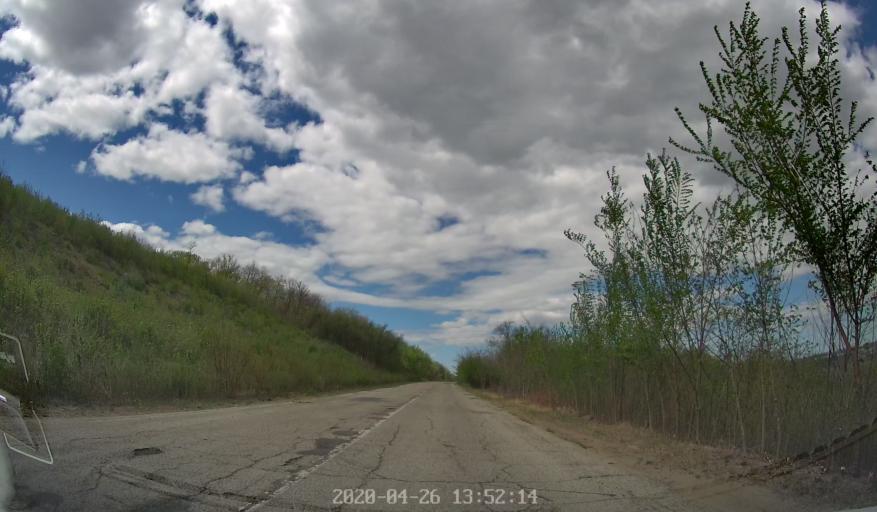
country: MD
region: Telenesti
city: Cocieri
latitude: 47.2715
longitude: 29.1199
